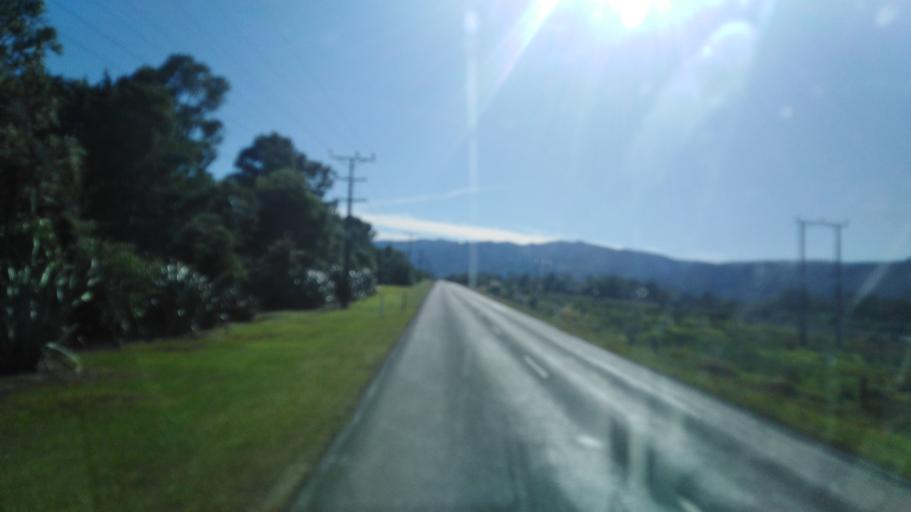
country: NZ
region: West Coast
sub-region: Buller District
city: Westport
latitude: -41.7408
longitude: 171.6965
